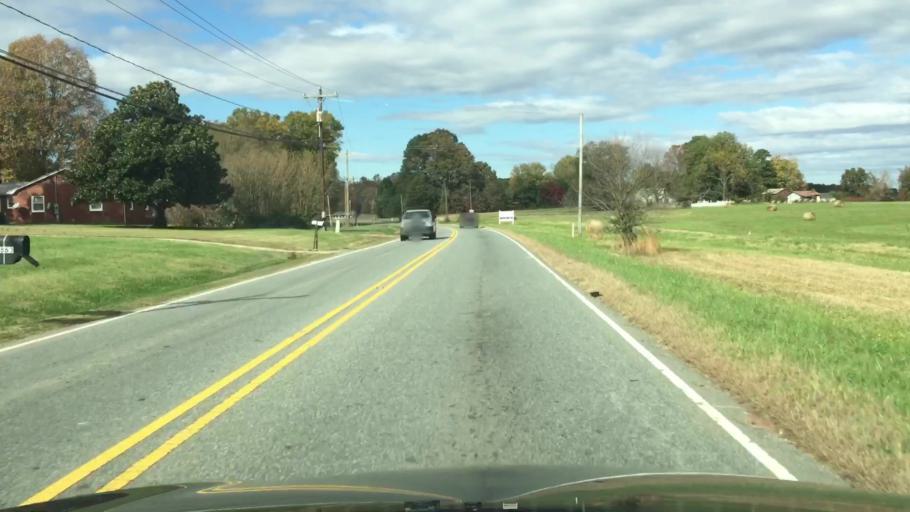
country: US
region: North Carolina
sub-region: Iredell County
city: Mooresville
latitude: 35.6309
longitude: -80.8244
